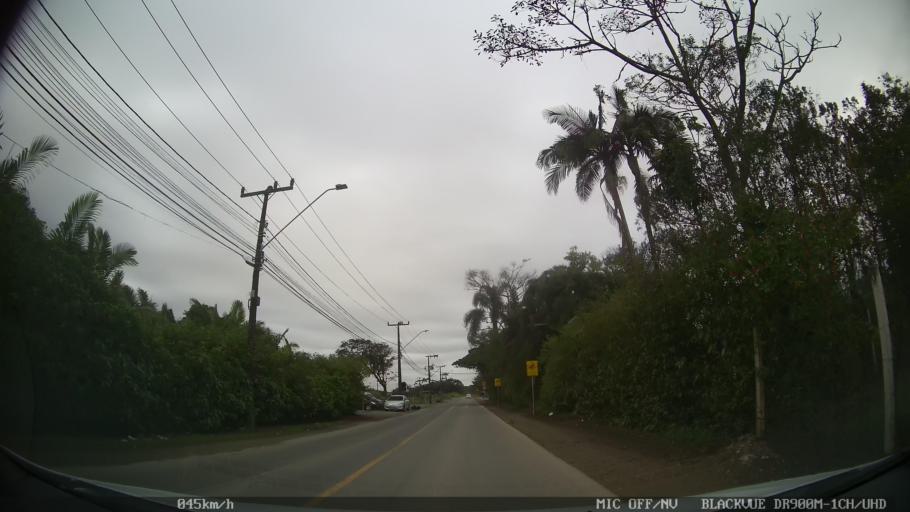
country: BR
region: Santa Catarina
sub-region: Joinville
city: Joinville
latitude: -26.2670
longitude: -48.9243
